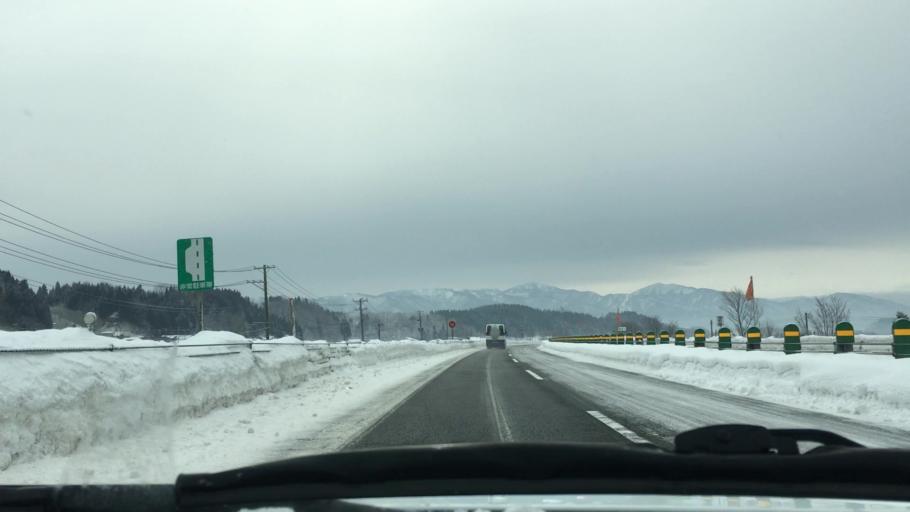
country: JP
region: Akita
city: Hanawa
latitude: 40.2949
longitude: 140.7550
